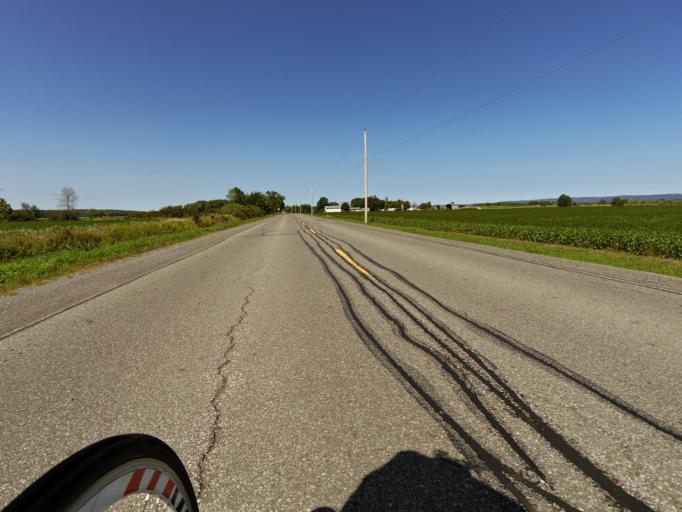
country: CA
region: Ontario
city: Bells Corners
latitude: 45.4056
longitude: -76.0263
